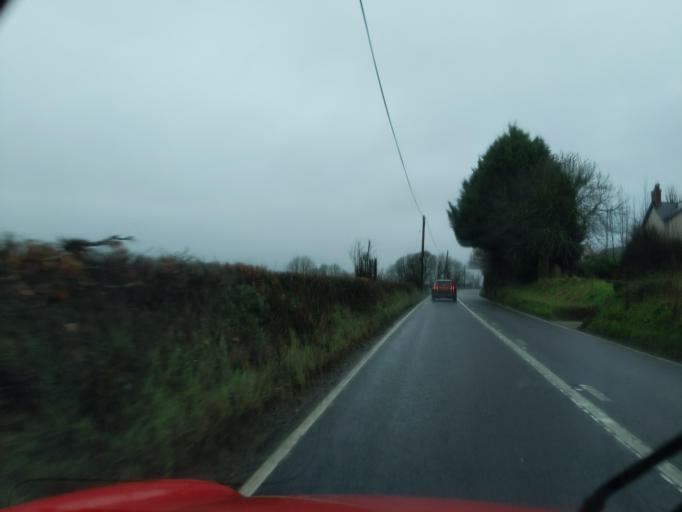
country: GB
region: England
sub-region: Cornwall
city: Launceston
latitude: 50.6047
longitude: -4.3387
